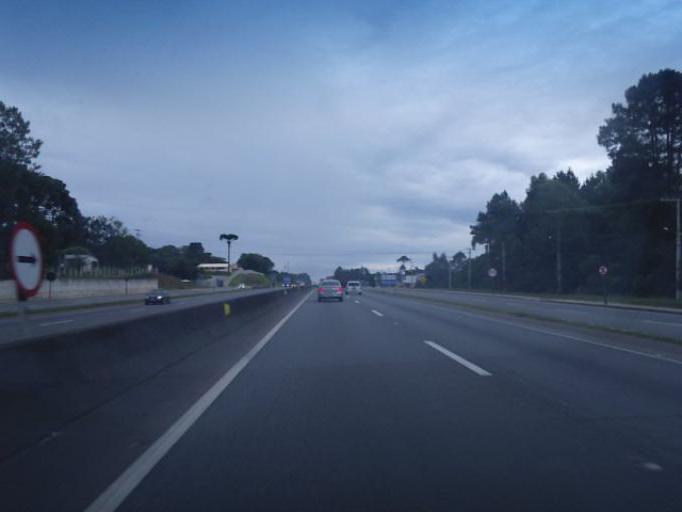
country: BR
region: Parana
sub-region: Sao Jose Dos Pinhais
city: Sao Jose dos Pinhais
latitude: -25.7045
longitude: -49.1419
